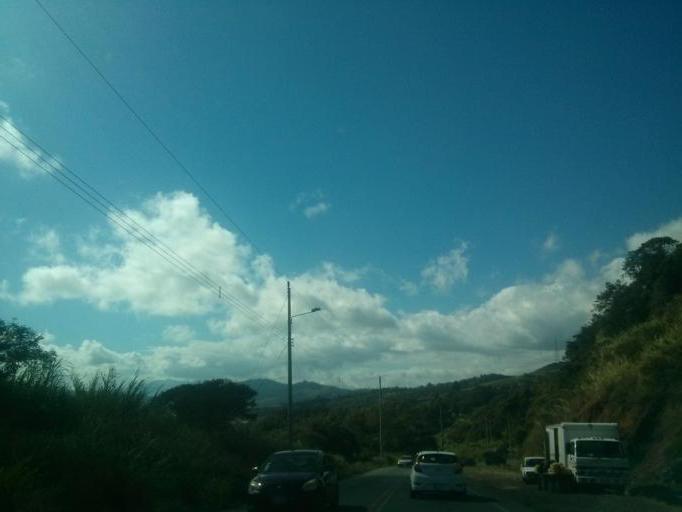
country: CR
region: Cartago
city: Cot
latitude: 9.8841
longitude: -83.8923
